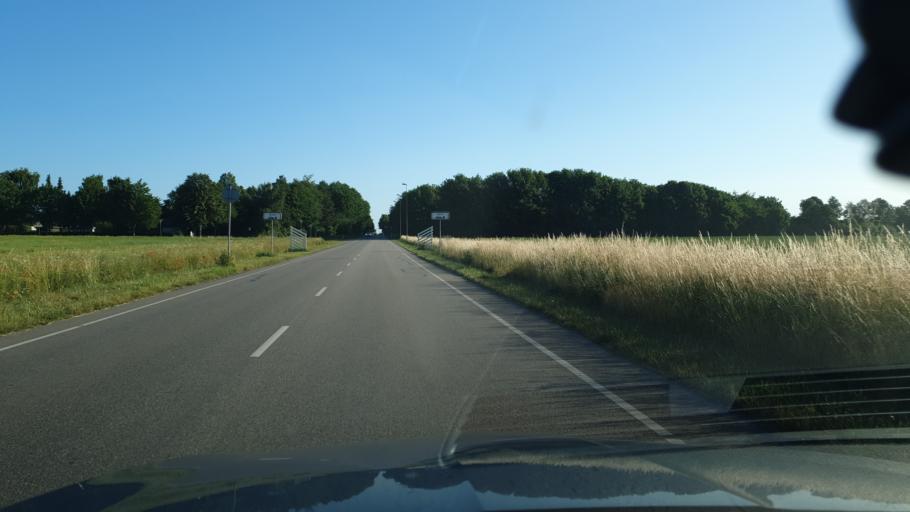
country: DK
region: Zealand
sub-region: Soro Kommune
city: Frederiksberg
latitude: 55.4055
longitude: 11.5639
